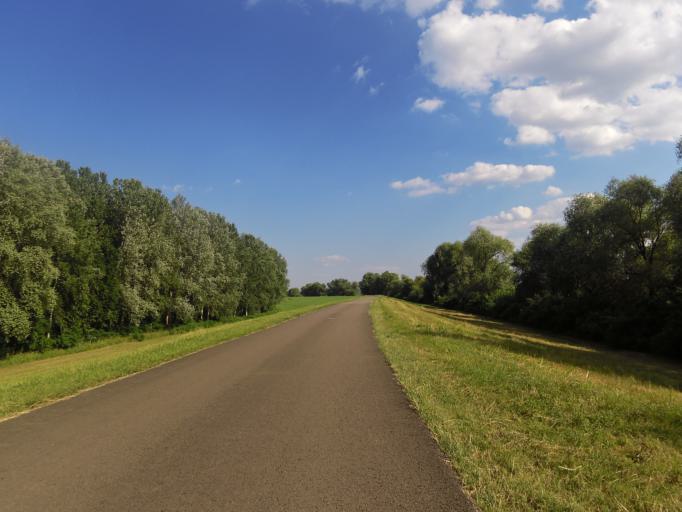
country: HU
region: Jasz-Nagykun-Szolnok
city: Abadszalok
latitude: 47.5051
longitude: 20.5968
